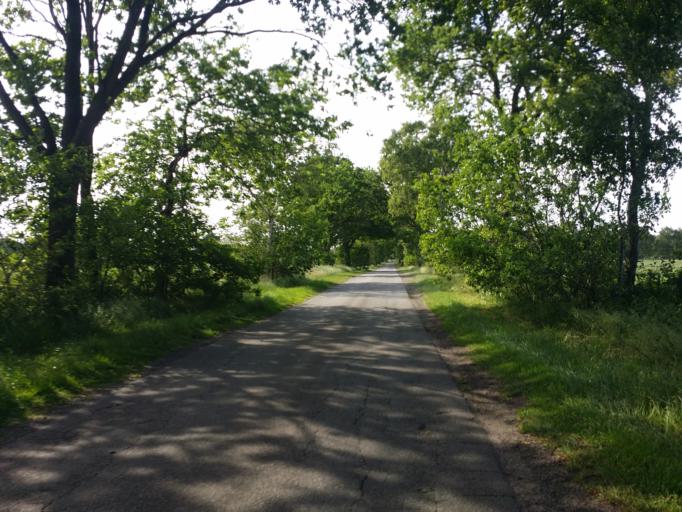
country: DE
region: Lower Saxony
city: Bockhorn
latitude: 53.3222
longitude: 8.0378
